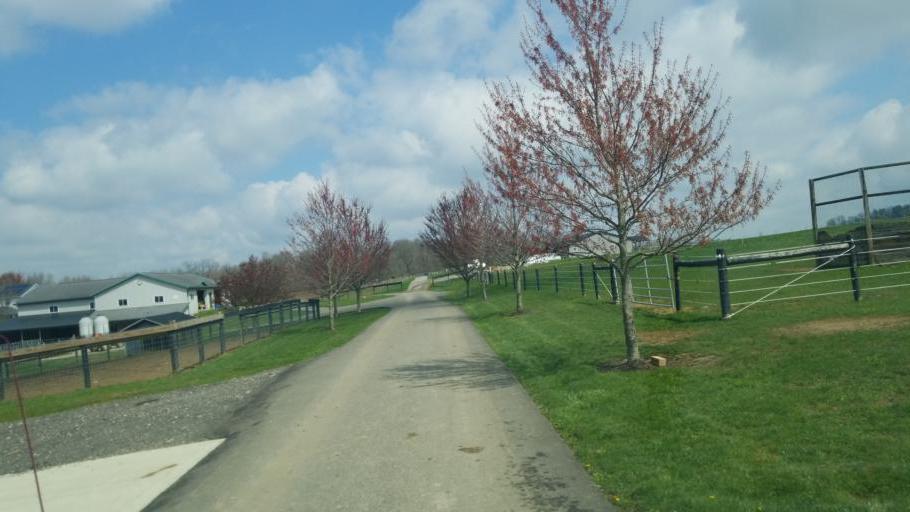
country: US
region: Ohio
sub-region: Wayne County
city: Apple Creek
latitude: 40.6829
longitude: -81.8325
